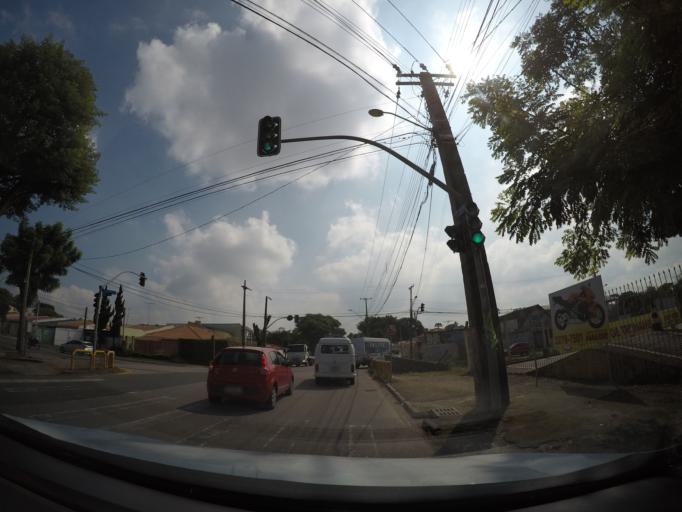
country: BR
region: Parana
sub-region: Sao Jose Dos Pinhais
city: Sao Jose dos Pinhais
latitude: -25.4909
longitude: -49.2552
